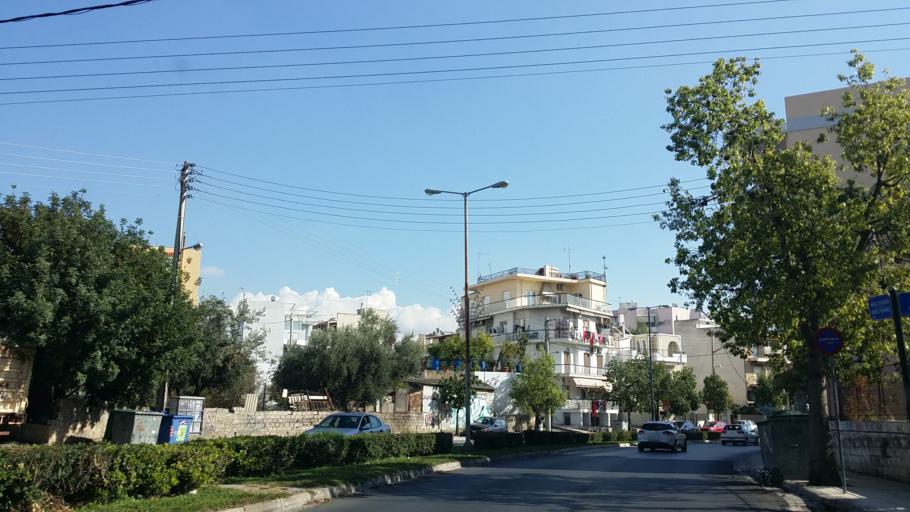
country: GR
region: Attica
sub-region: Nomarchia Athinas
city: Ilion
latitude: 38.0224
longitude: 23.7075
